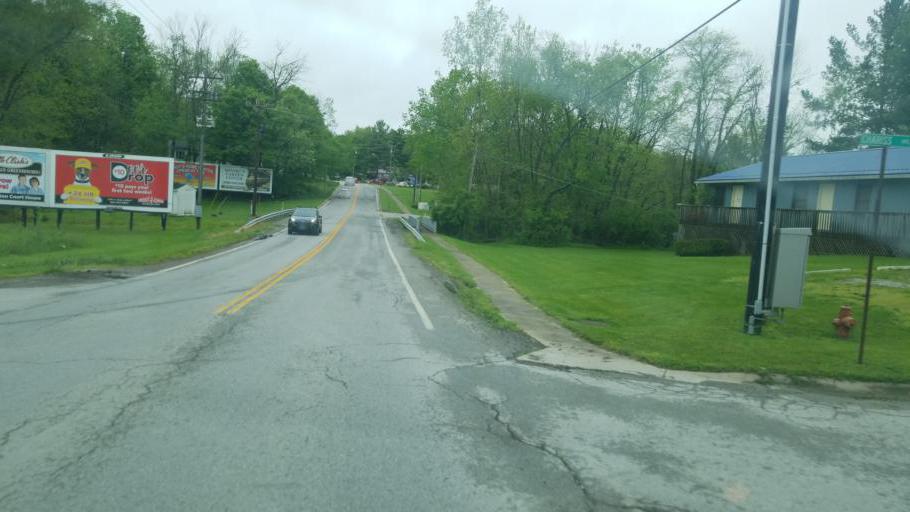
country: US
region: Ohio
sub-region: Highland County
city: Hillsboro
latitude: 39.2164
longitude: -83.6160
